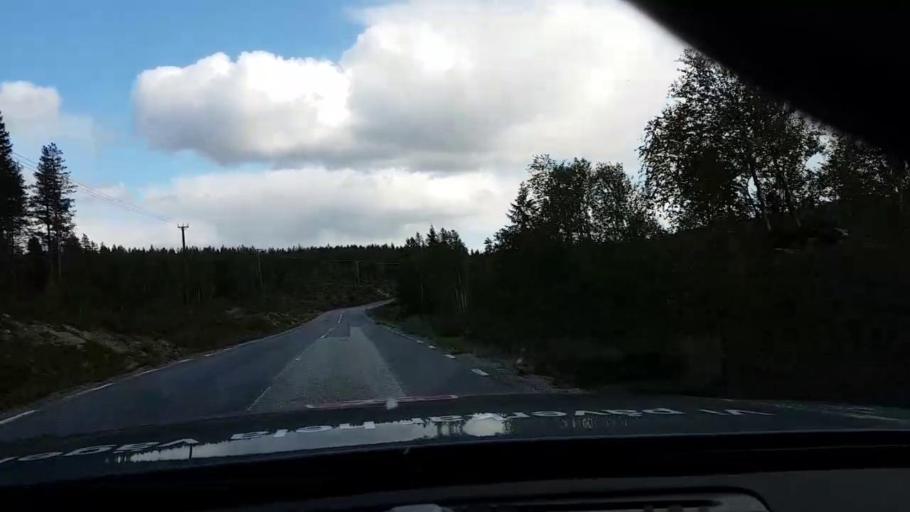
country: SE
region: Vaesterbotten
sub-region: Asele Kommun
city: Asele
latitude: 63.8011
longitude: 17.5533
